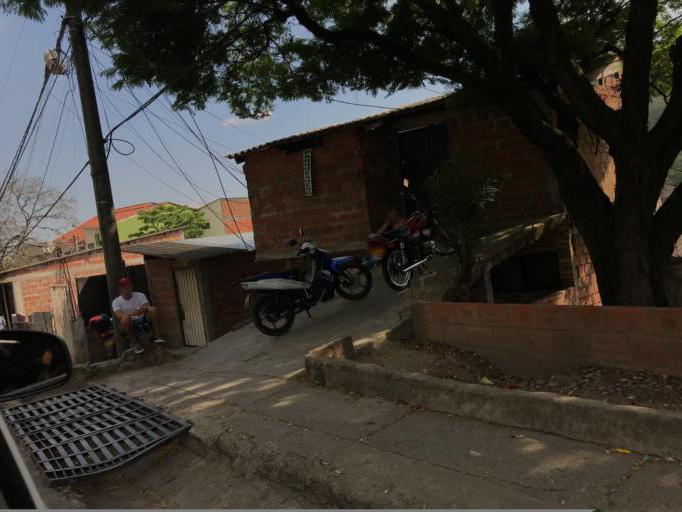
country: CO
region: Valle del Cauca
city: Cali
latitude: 3.4507
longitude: -76.5638
